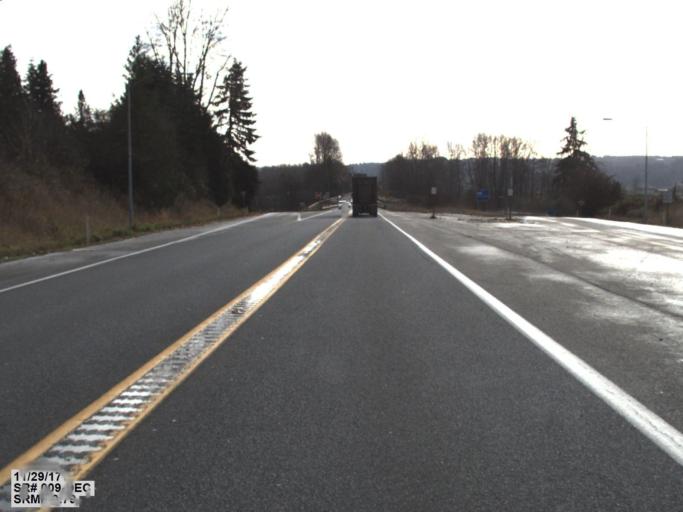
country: US
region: Washington
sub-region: Snohomish County
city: Snohomish
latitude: 47.9187
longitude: -122.1084
